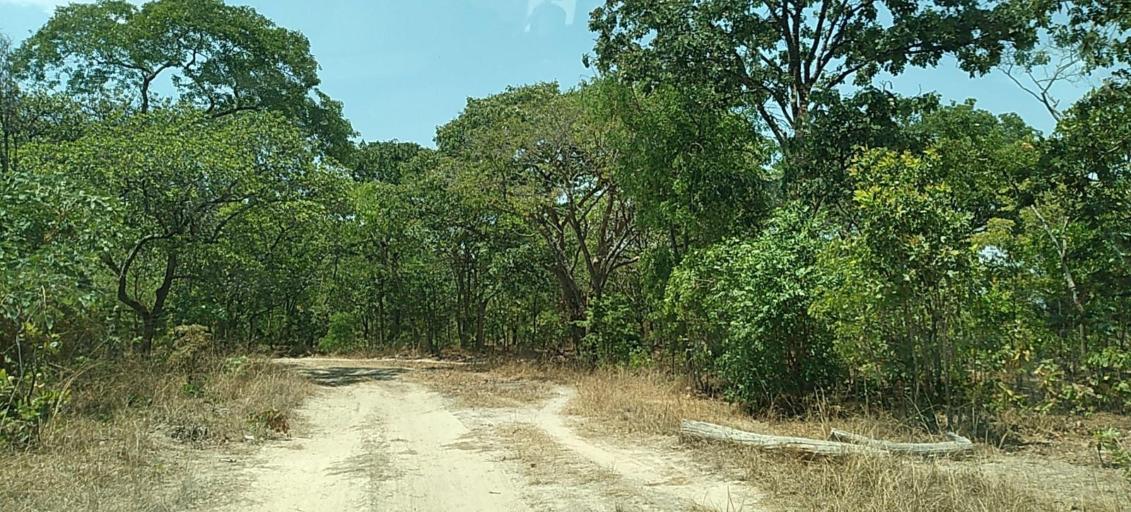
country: ZM
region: Central
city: Kapiri Mposhi
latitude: -13.6674
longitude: 28.4918
